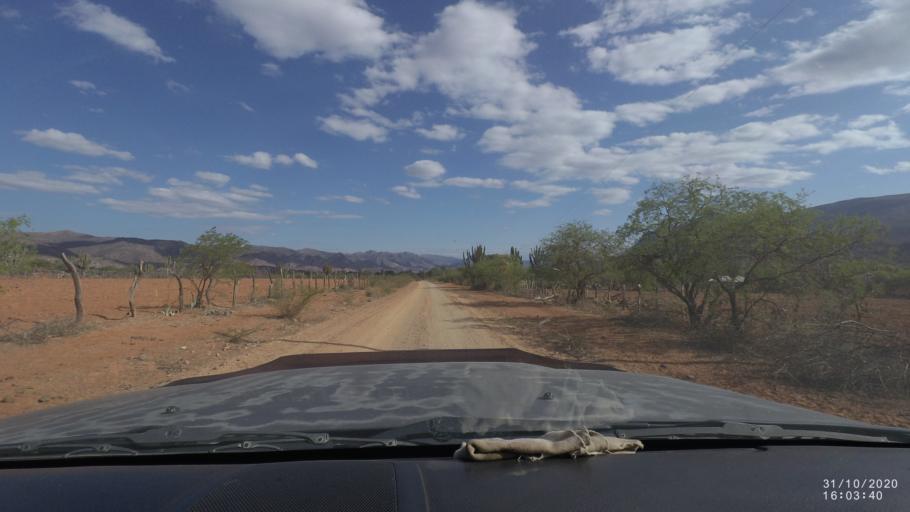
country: BO
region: Chuquisaca
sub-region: Provincia Zudanez
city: Mojocoya
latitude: -18.3538
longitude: -64.6521
